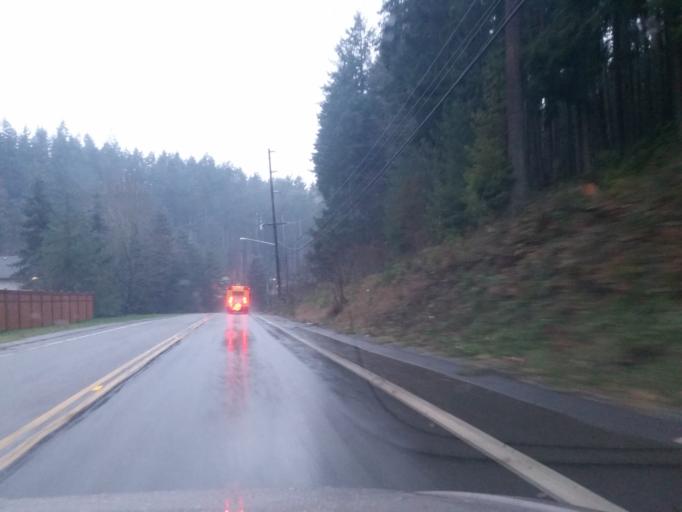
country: US
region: Washington
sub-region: Snohomish County
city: Meadowdale
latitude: 47.8733
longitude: -122.3100
